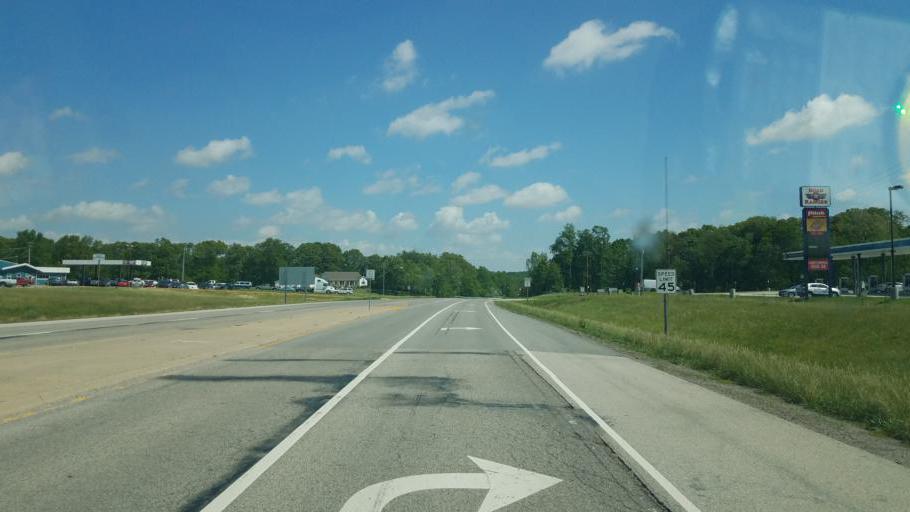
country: US
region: Illinois
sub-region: Clark County
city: Marshall
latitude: 39.4239
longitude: -87.6929
